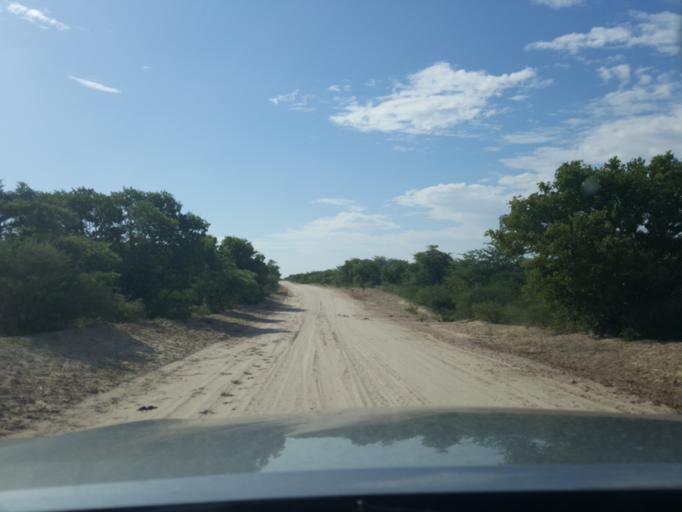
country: BW
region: Kweneng
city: Khudumelapye
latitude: -23.4921
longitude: 24.7001
